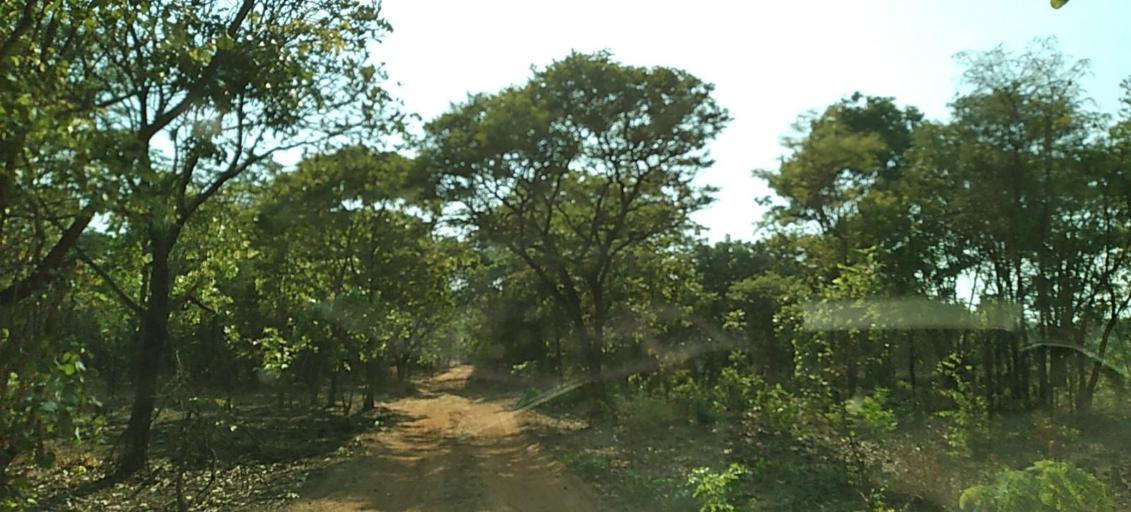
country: ZM
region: Copperbelt
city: Kalulushi
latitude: -13.0050
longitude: 27.7556
